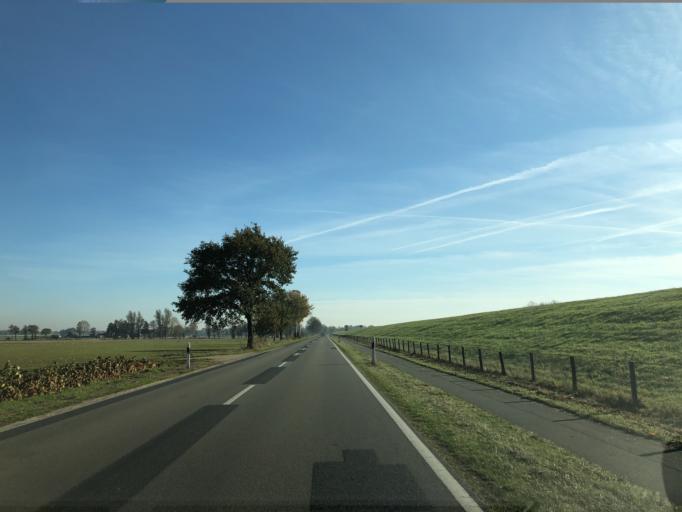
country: DE
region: Lower Saxony
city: Rhede
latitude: 53.0593
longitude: 7.2987
